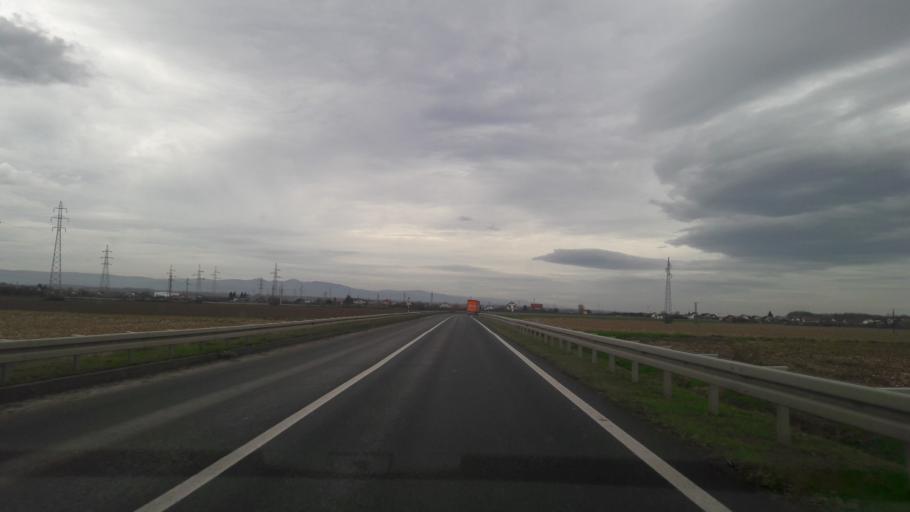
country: HR
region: Osjecko-Baranjska
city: Velimirovac
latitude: 45.5104
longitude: 18.1072
